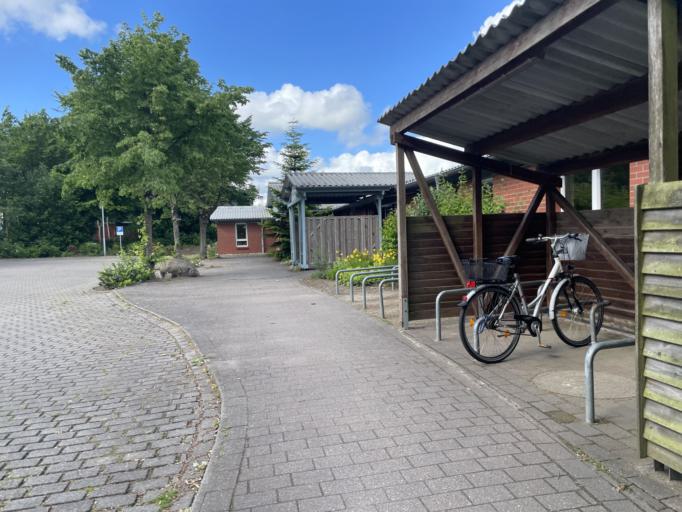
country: DE
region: Schleswig-Holstein
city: Mildstedt
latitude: 54.4671
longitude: 9.1001
